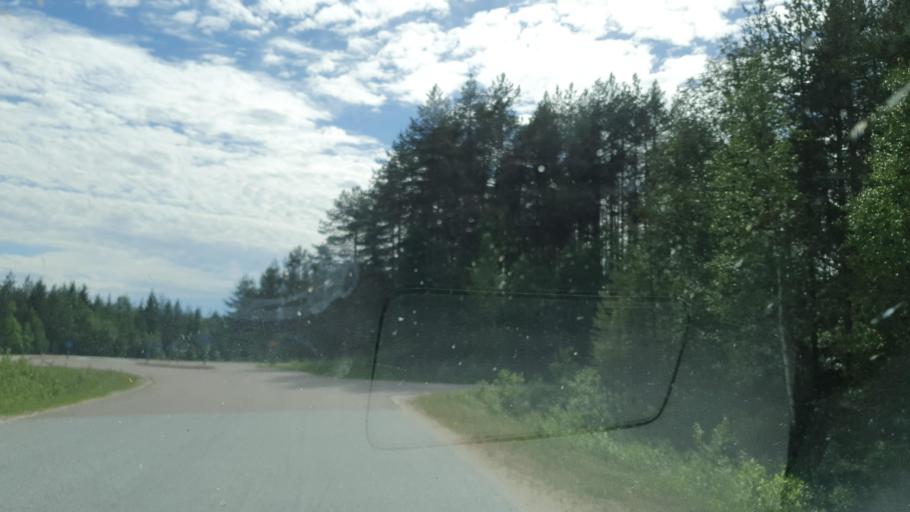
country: FI
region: Kainuu
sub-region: Kehys-Kainuu
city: Kuhmo
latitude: 64.4596
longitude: 29.5328
